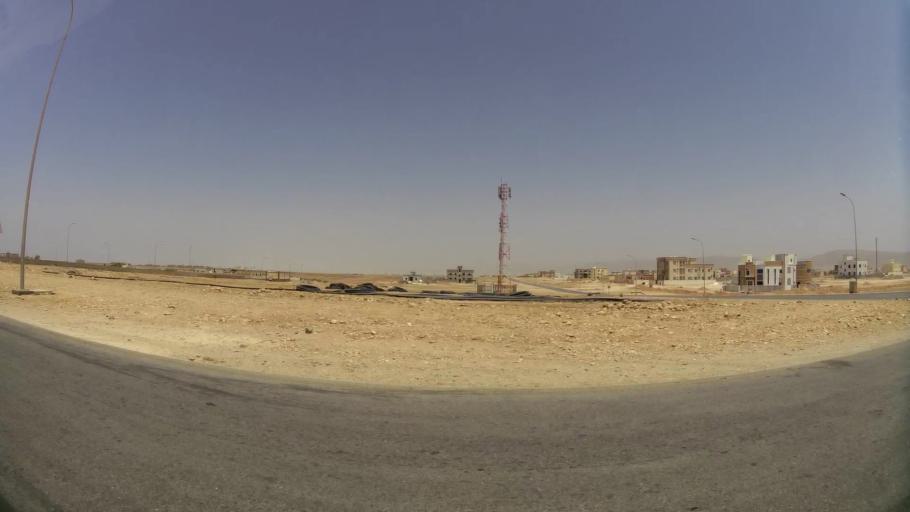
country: OM
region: Zufar
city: Salalah
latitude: 17.0913
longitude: 54.1869
